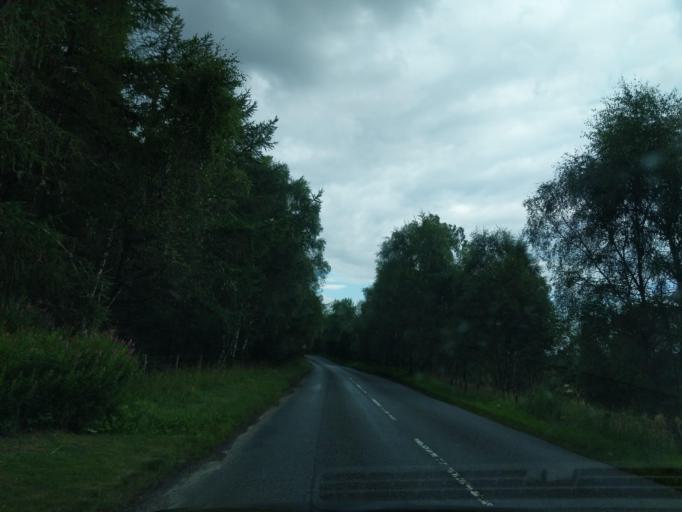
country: GB
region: Scotland
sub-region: Highland
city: Aviemore
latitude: 57.2887
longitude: -3.7969
